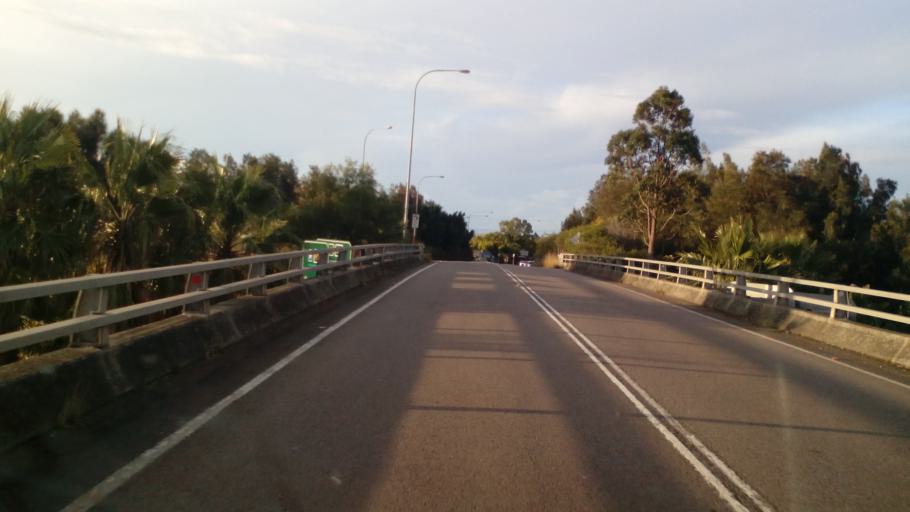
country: AU
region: New South Wales
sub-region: Newcastle
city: Beresfield
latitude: -32.8121
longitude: 151.6657
